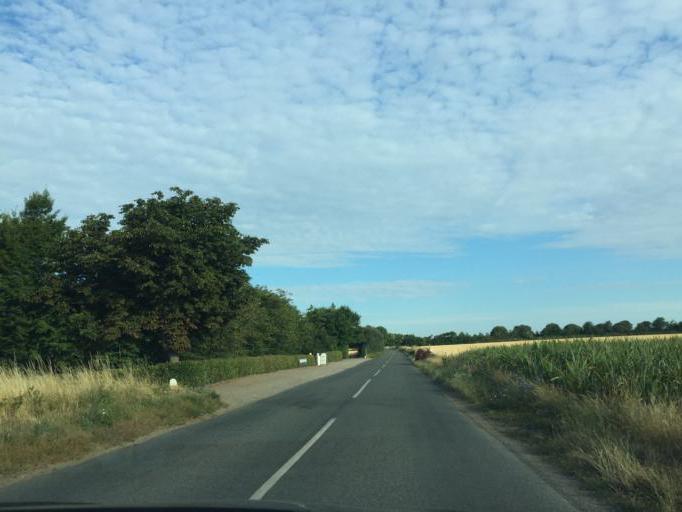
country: DK
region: South Denmark
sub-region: Assens Kommune
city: Harby
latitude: 55.1557
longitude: 10.0049
